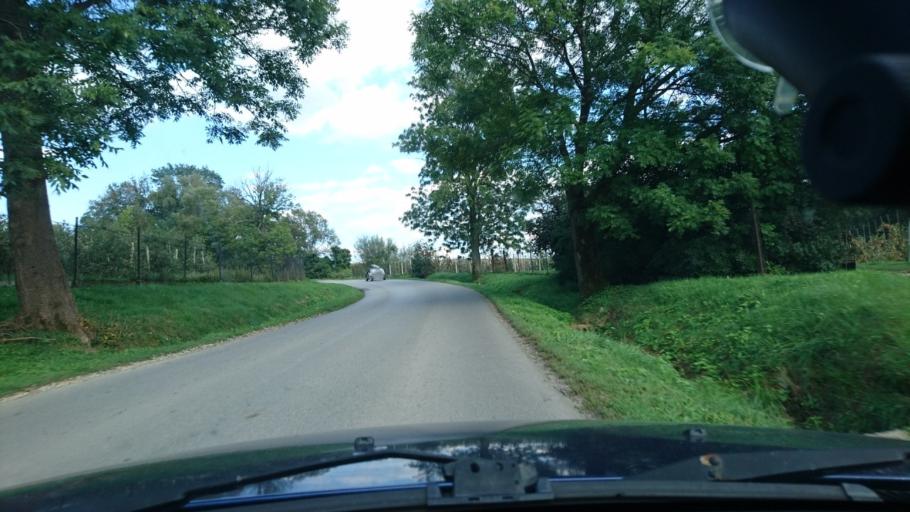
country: PL
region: Silesian Voivodeship
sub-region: Powiat bielski
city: Mazancowice
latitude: 49.8525
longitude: 18.9516
